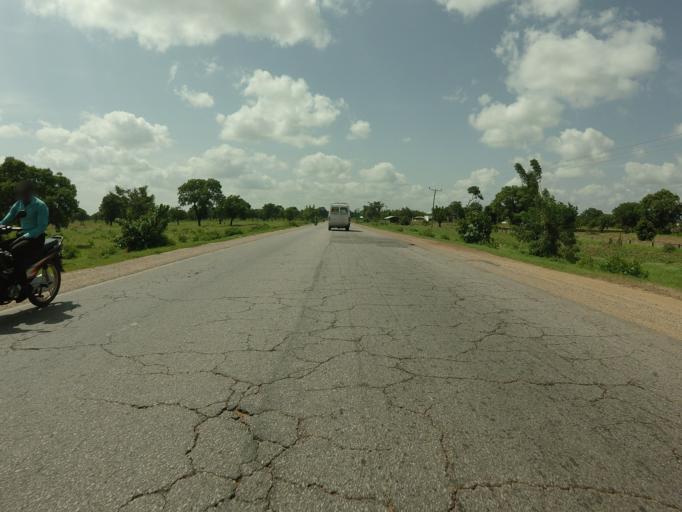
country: GH
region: Northern
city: Savelugu
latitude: 9.5695
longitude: -0.8352
